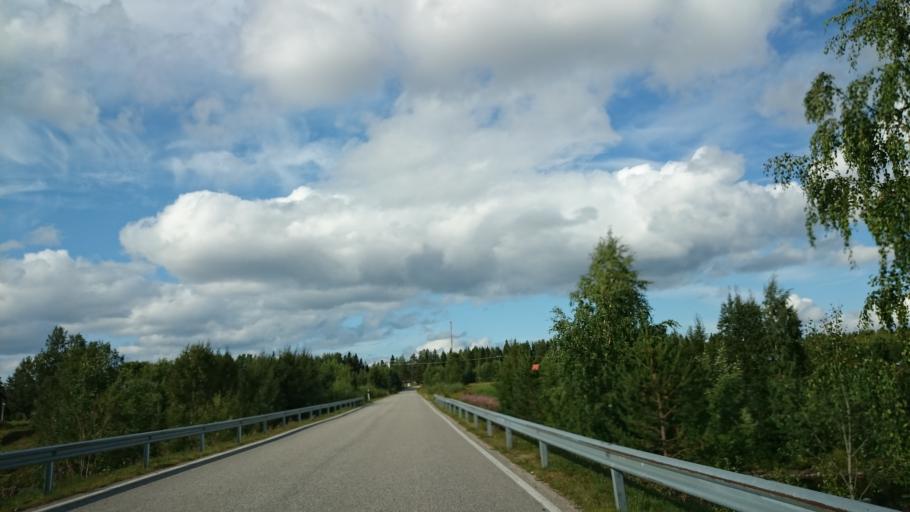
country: FI
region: Kainuu
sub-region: Kehys-Kainuu
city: Suomussalmi
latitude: 64.7436
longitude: 29.4397
